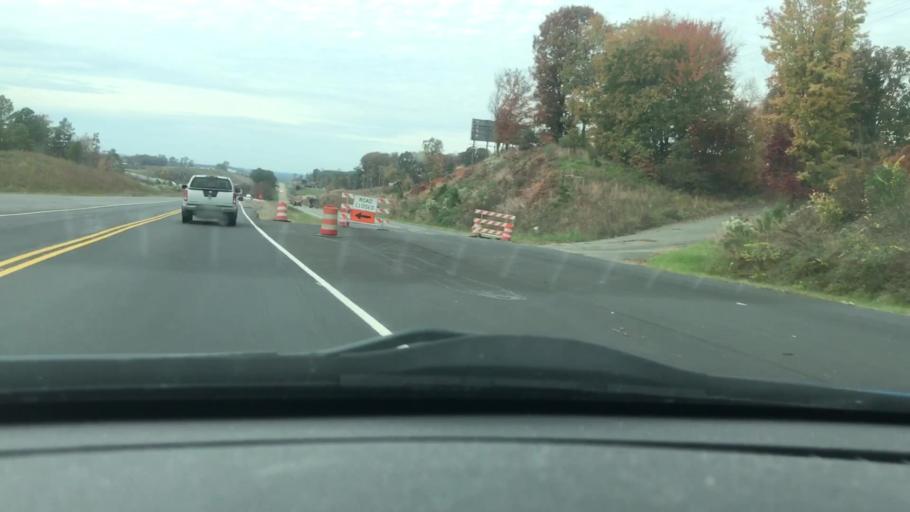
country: US
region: North Carolina
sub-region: Randolph County
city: Asheboro
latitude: 35.6949
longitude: -79.8622
